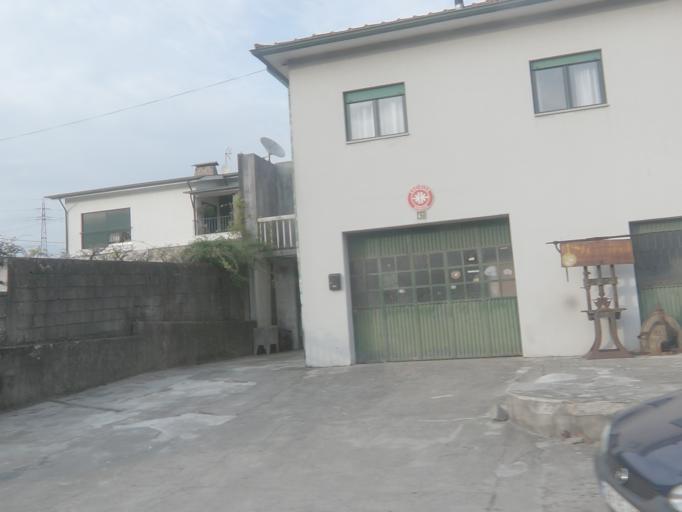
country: PT
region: Porto
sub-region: Valongo
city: Campo
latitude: 41.1847
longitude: -8.4857
